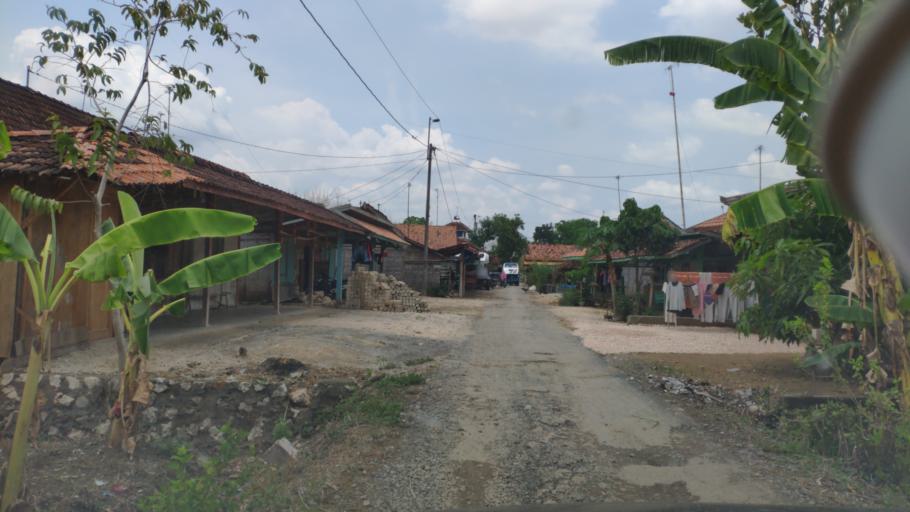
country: ID
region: Central Java
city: Gumiring
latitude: -7.0418
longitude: 111.3911
